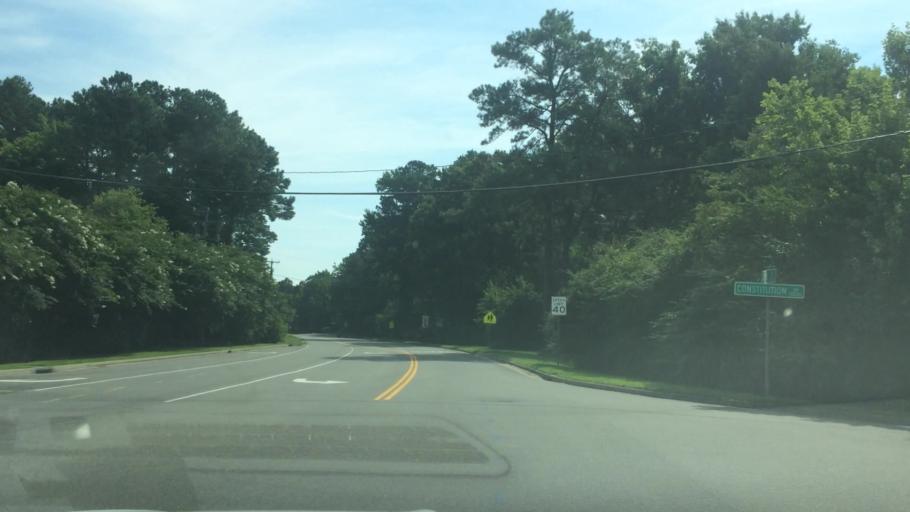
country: US
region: Virginia
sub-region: York County
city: Yorktown
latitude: 37.1607
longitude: -76.4610
